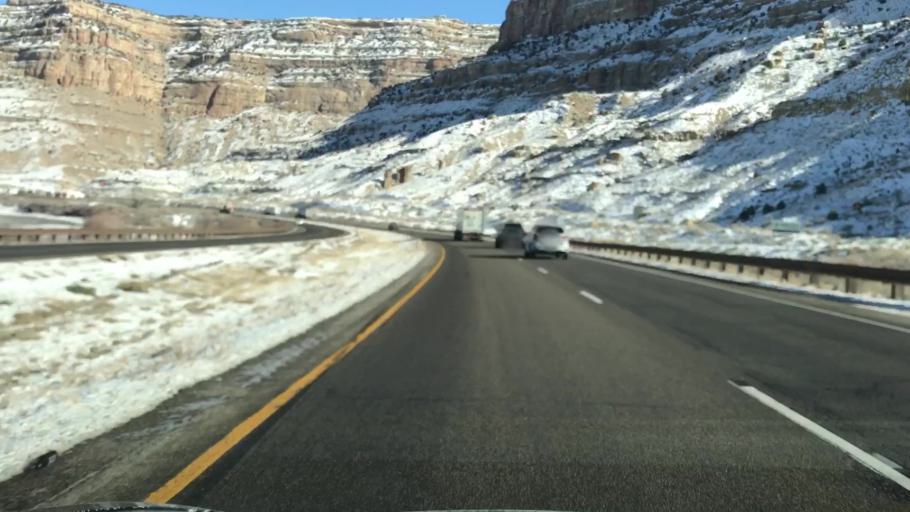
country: US
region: Colorado
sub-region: Mesa County
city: Palisade
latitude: 39.1513
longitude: -108.3047
